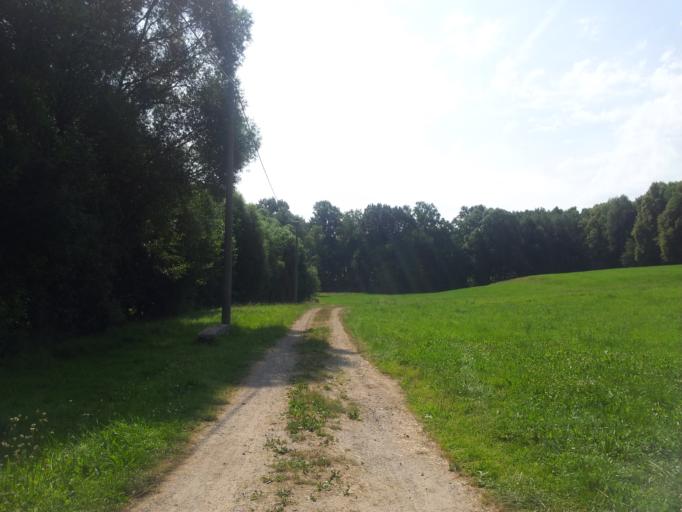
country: DE
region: Saxony
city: Panschwitz-Kuckau
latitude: 51.2143
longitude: 14.1958
